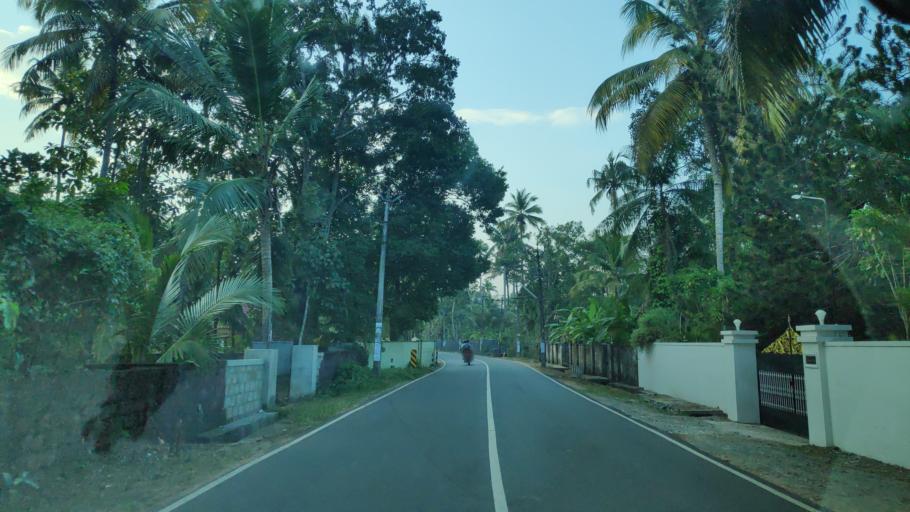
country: IN
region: Kerala
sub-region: Alappuzha
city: Shertallai
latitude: 9.6811
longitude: 76.3687
